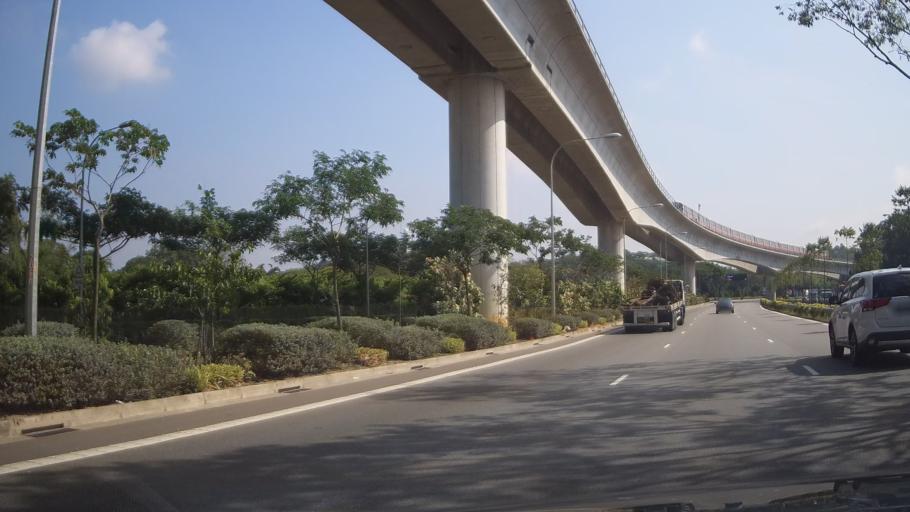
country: MY
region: Johor
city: Johor Bahru
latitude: 1.3250
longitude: 103.6648
